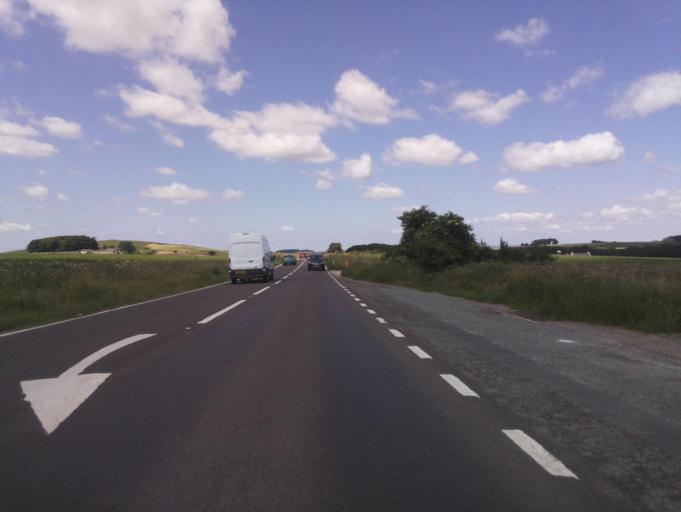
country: GB
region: England
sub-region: Derbyshire
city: Bakewell
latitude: 53.1513
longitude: -1.7678
